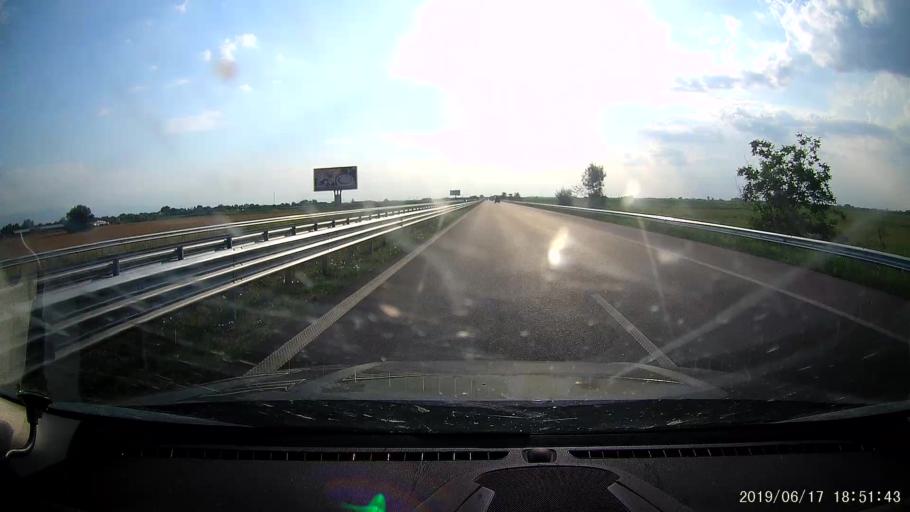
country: BG
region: Plovdiv
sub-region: Obshtina Rakovski
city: Rakovski
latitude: 42.2142
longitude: 24.9623
